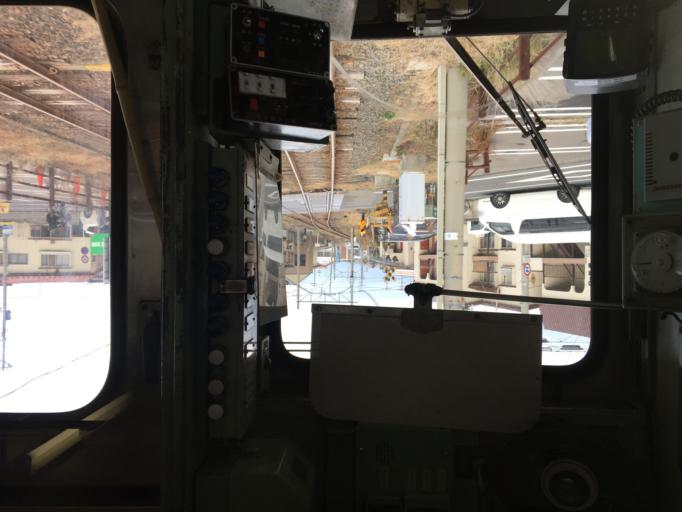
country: JP
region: Aomori
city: Hirosaki
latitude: 40.5842
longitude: 140.4704
